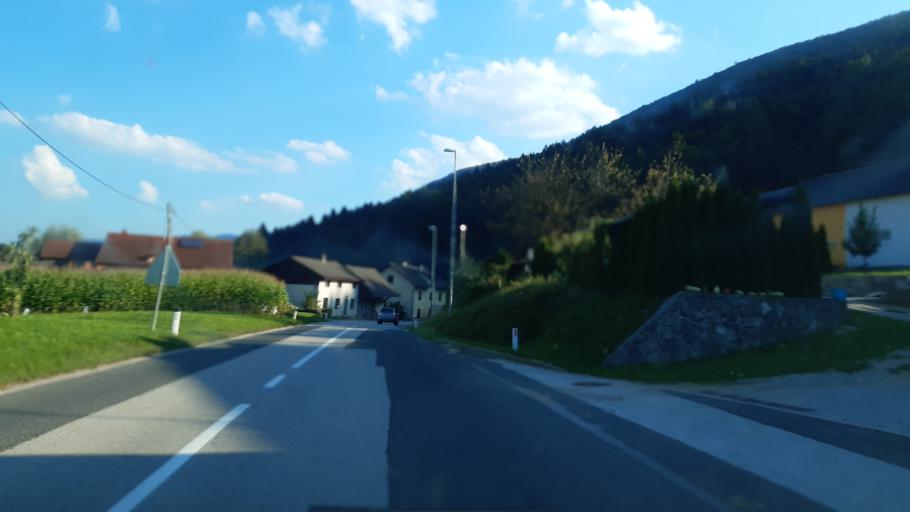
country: SI
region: Dolenjske Toplice
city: Dolenjske Toplice
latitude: 45.7509
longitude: 15.0354
